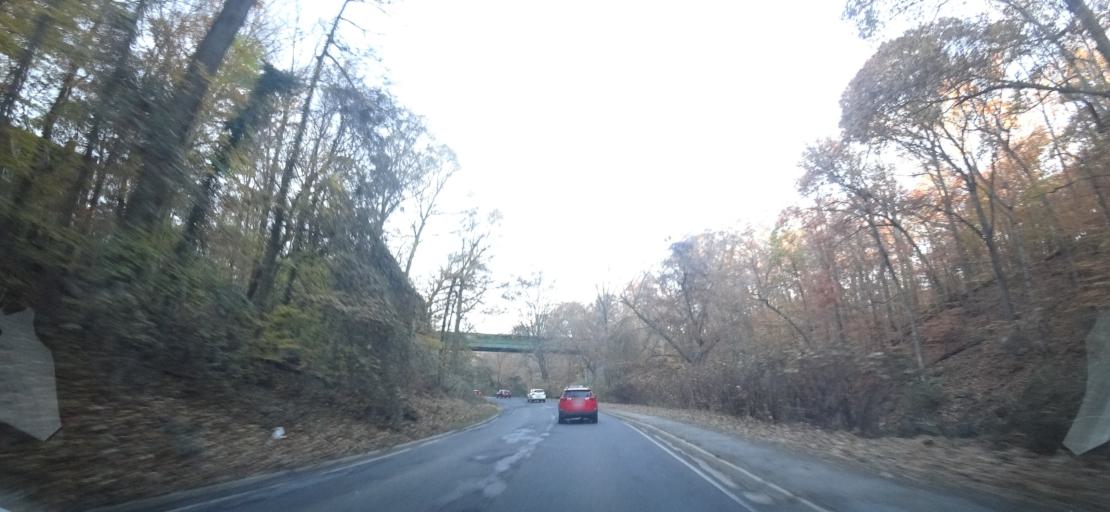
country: US
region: Washington, D.C.
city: Washington, D.C.
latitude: 38.9362
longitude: -77.0448
